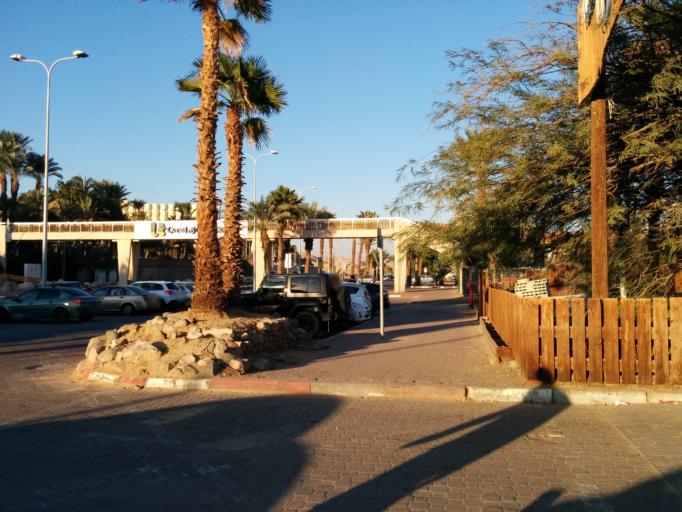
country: IL
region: Southern District
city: Eilat
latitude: 29.5127
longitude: 34.9246
